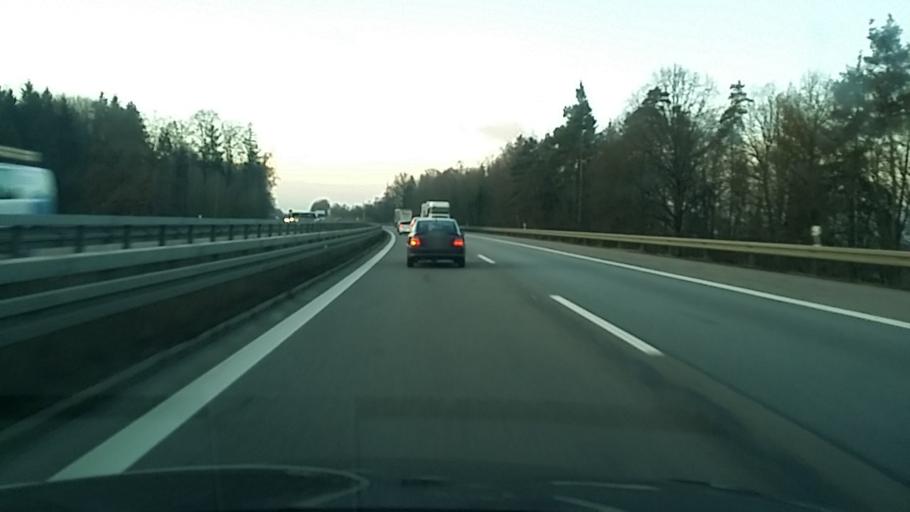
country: DE
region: Bavaria
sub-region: Upper Palatinate
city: Brunn
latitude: 49.0680
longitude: 11.9154
